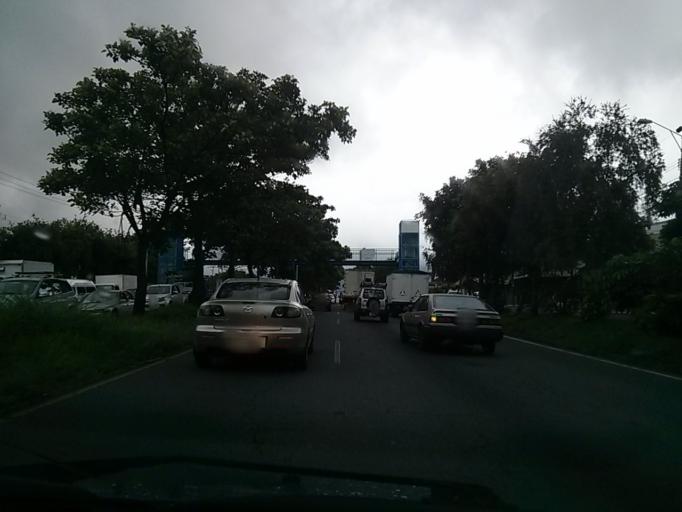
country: CR
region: San Jose
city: San Felipe
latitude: 9.9164
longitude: -84.1062
